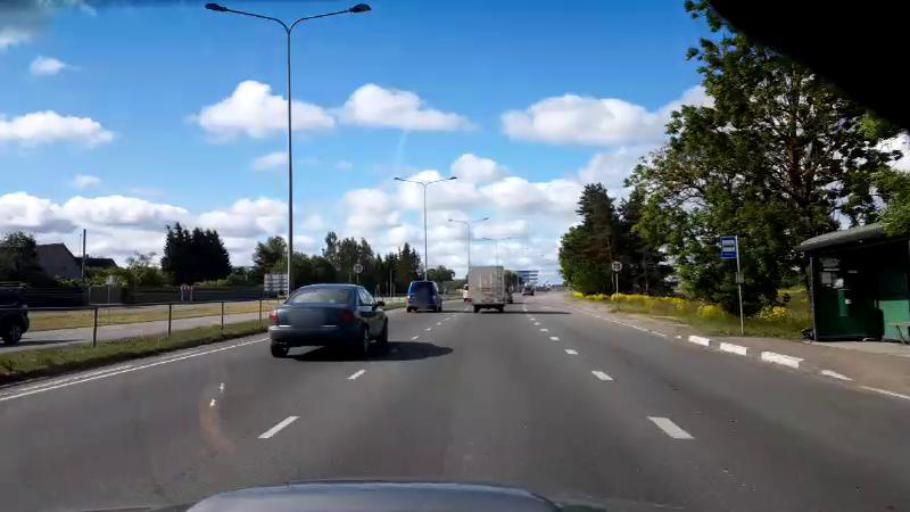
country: EE
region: Harju
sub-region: Saue vald
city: Laagri
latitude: 59.3483
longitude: 24.6253
